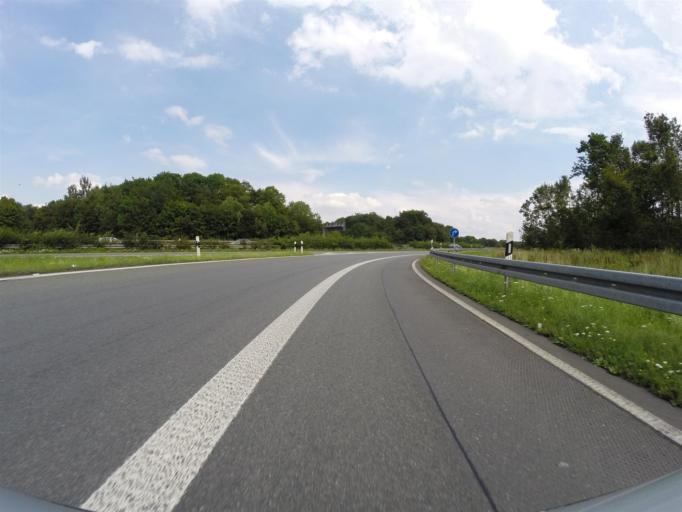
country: DE
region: North Rhine-Westphalia
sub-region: Regierungsbezirk Detmold
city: Wunnenberg
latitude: 51.5747
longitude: 8.7335
